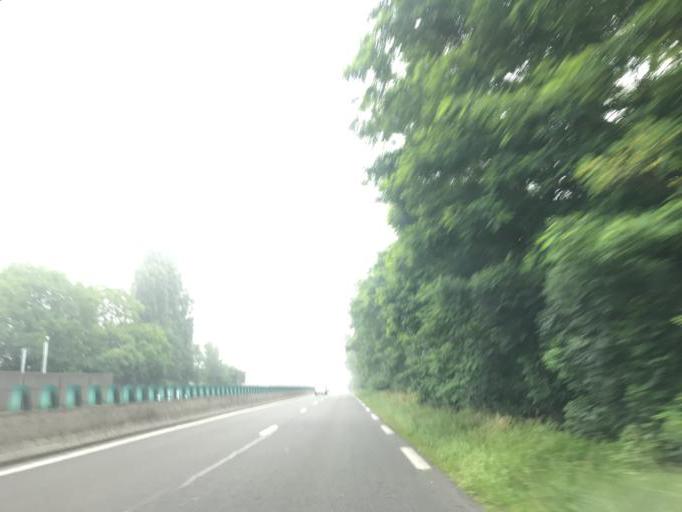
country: FR
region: Ile-de-France
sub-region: Departement de Seine-et-Marne
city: Lagny-sur-Marne
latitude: 48.8709
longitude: 2.7151
